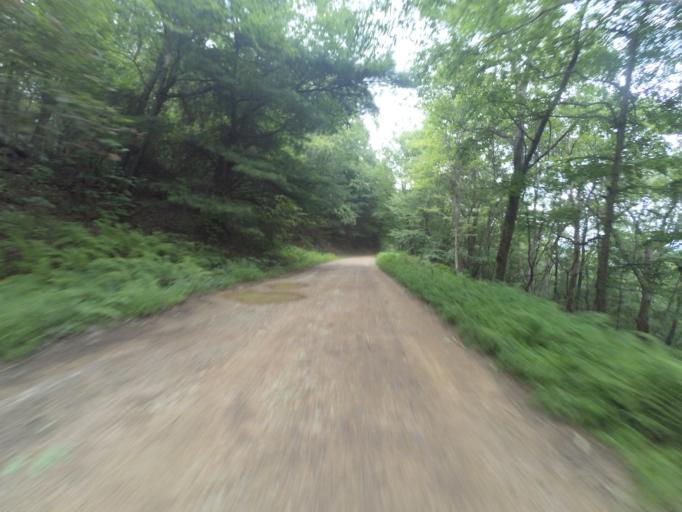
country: US
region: Pennsylvania
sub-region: Centre County
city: Boalsburg
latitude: 40.7099
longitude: -77.7730
